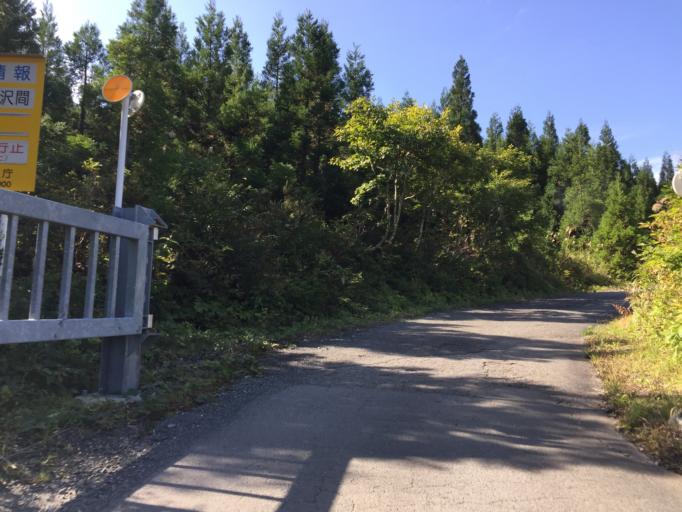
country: JP
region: Yamagata
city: Yonezawa
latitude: 37.8120
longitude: 140.2516
